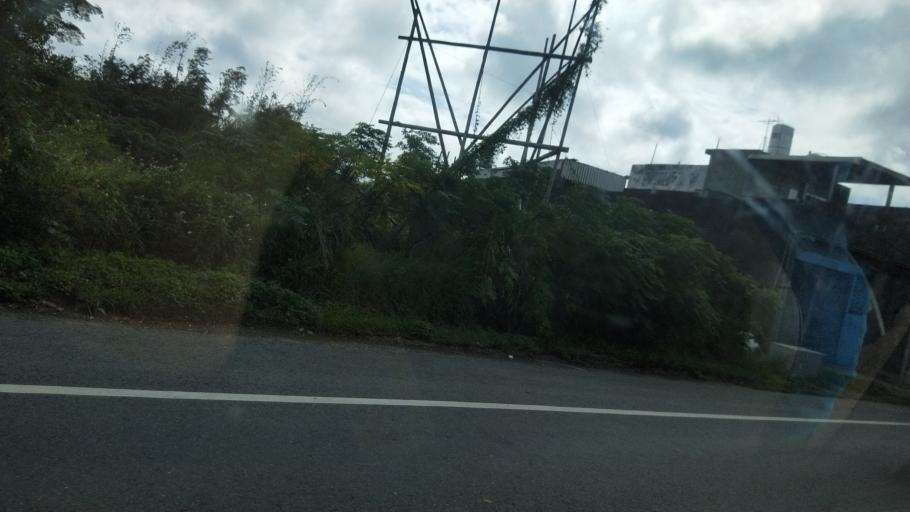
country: TW
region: Taiwan
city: Taoyuan City
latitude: 25.0075
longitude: 121.1324
